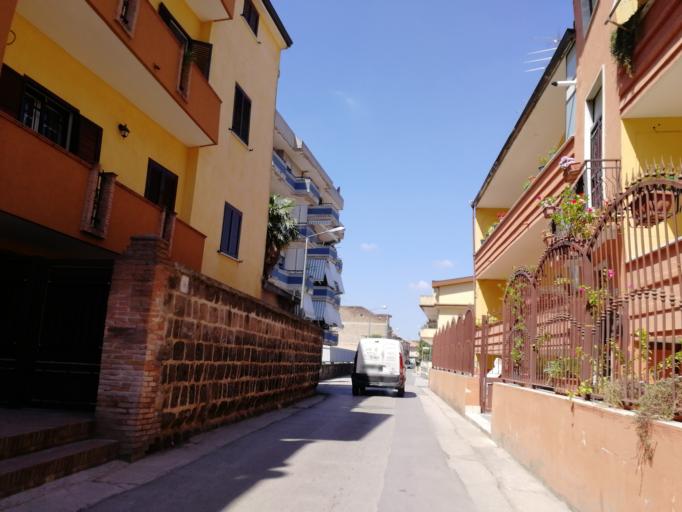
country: IT
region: Campania
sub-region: Provincia di Caserta
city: San Prisco
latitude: 41.0886
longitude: 14.2771
